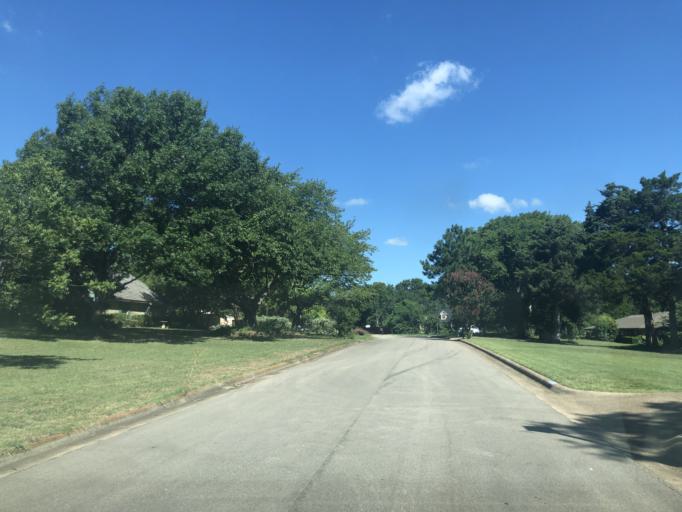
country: US
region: Texas
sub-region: Dallas County
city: Duncanville
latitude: 32.6346
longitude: -96.9321
